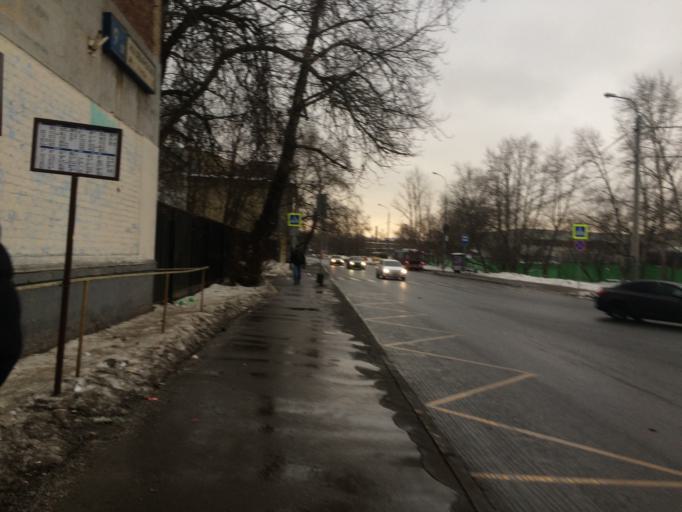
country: RU
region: Moscow
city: Mar'ino
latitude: 55.6606
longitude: 37.7202
